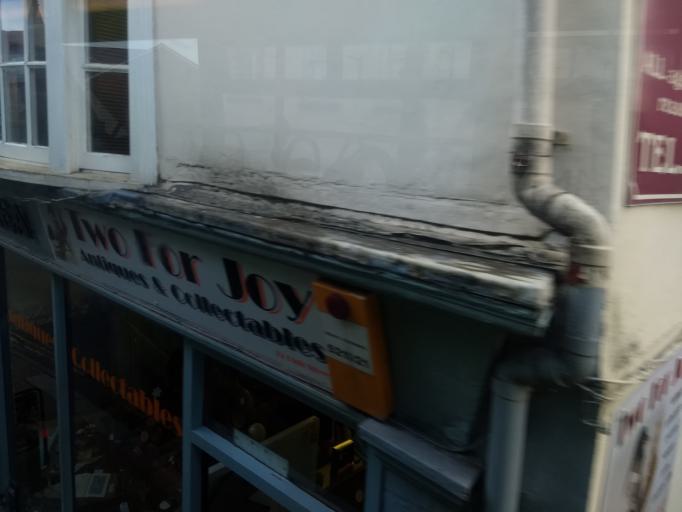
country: GB
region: England
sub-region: Isle of Wight
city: Newport
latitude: 50.6991
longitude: -1.2980
